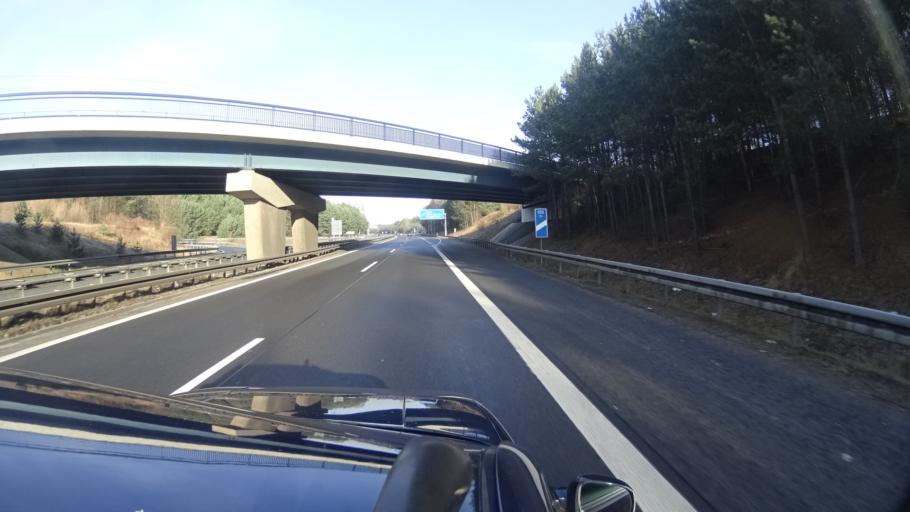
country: DE
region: Berlin
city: Heiligensee
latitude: 52.6518
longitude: 13.2440
